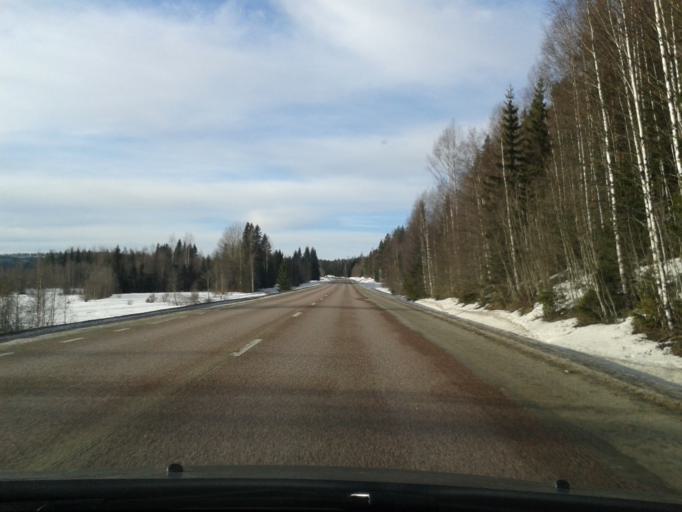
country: SE
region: Vaesternorrland
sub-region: OErnskoeldsviks Kommun
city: Bredbyn
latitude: 63.3926
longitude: 18.3364
